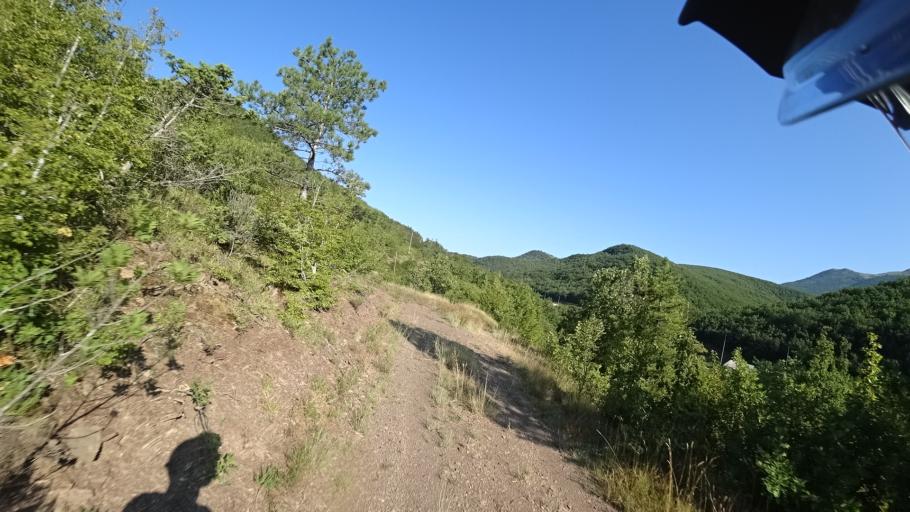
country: HR
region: Sibensko-Kniniska
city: Knin
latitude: 44.1231
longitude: 16.1956
